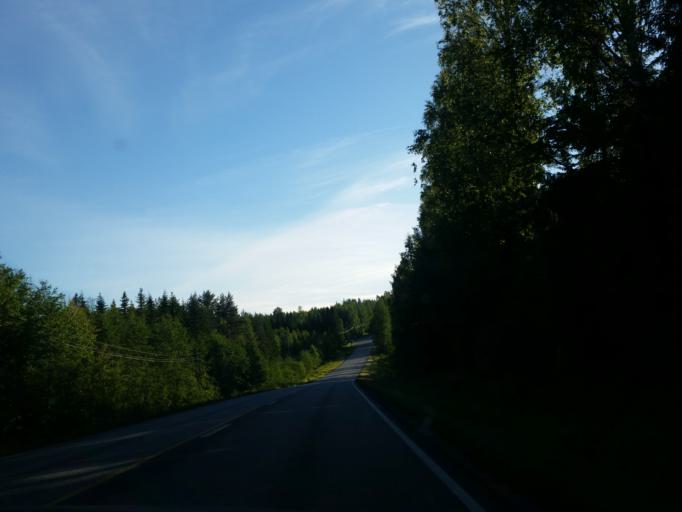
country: FI
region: Northern Savo
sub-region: Kuopio
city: Kuopio
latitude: 62.8446
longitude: 27.4305
